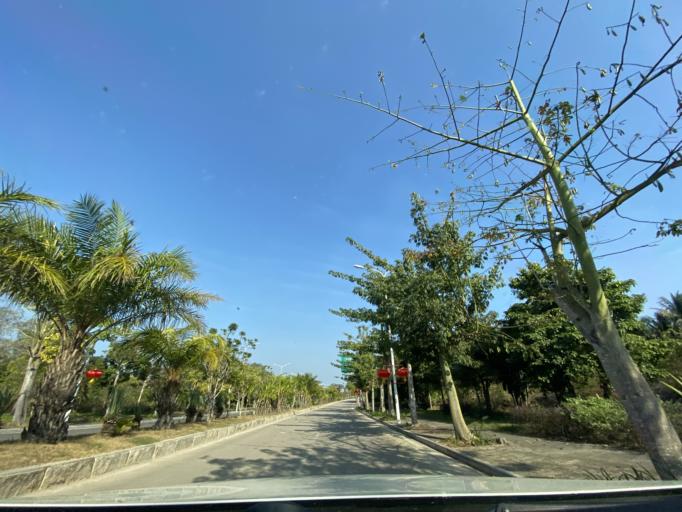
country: CN
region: Hainan
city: Haitangwan
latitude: 18.4032
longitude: 109.7668
